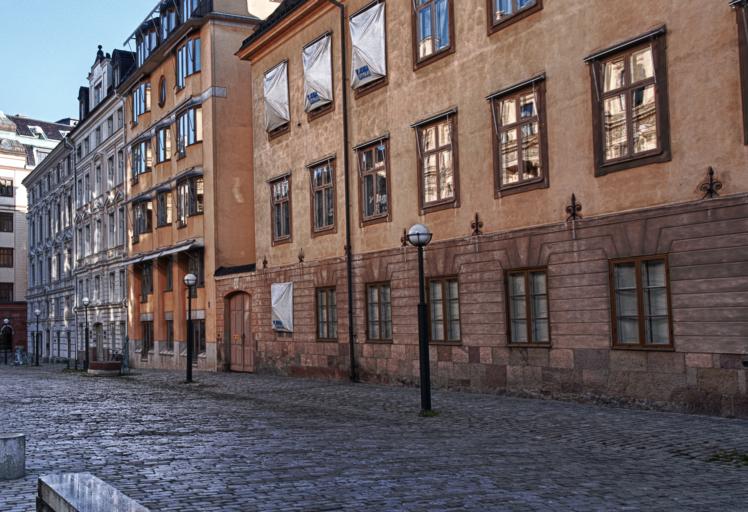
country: SE
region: Stockholm
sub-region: Stockholms Kommun
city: Stockholm
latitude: 59.3305
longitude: 18.0752
